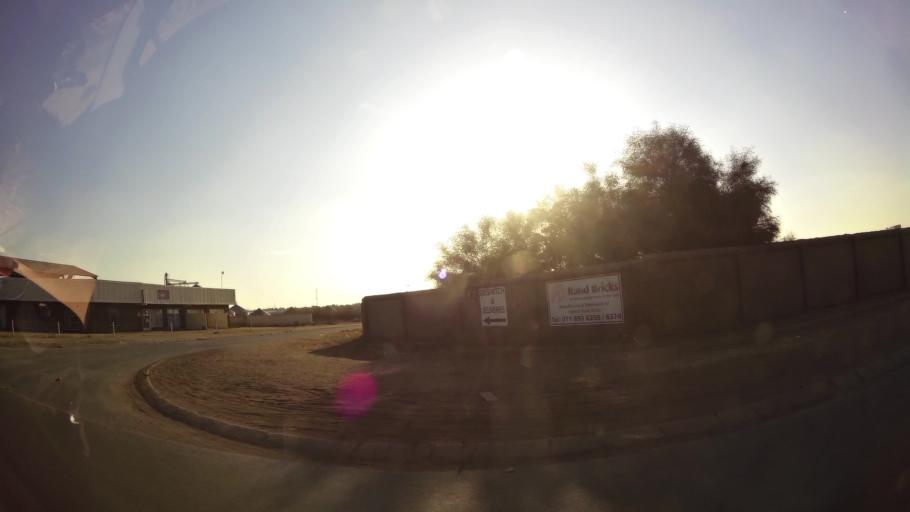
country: ZA
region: Gauteng
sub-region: West Rand District Municipality
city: Randfontein
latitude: -26.1960
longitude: 27.6901
